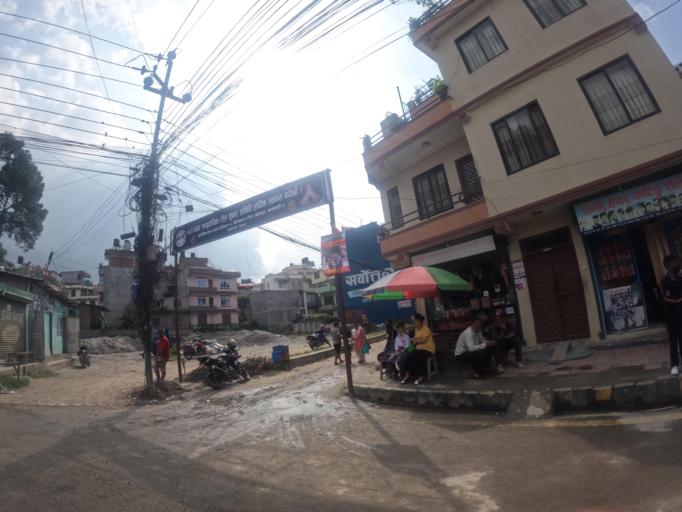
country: NP
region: Central Region
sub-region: Bagmati Zone
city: Bhaktapur
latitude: 27.6648
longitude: 85.3863
